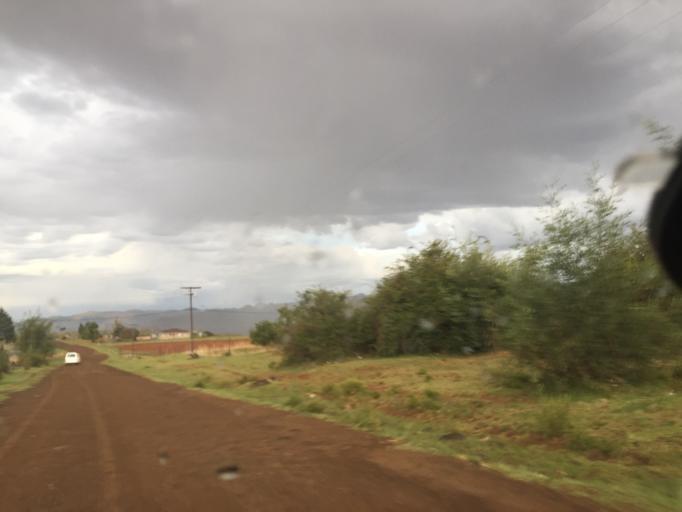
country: LS
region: Leribe
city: Leribe
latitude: -29.1543
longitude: 28.0376
